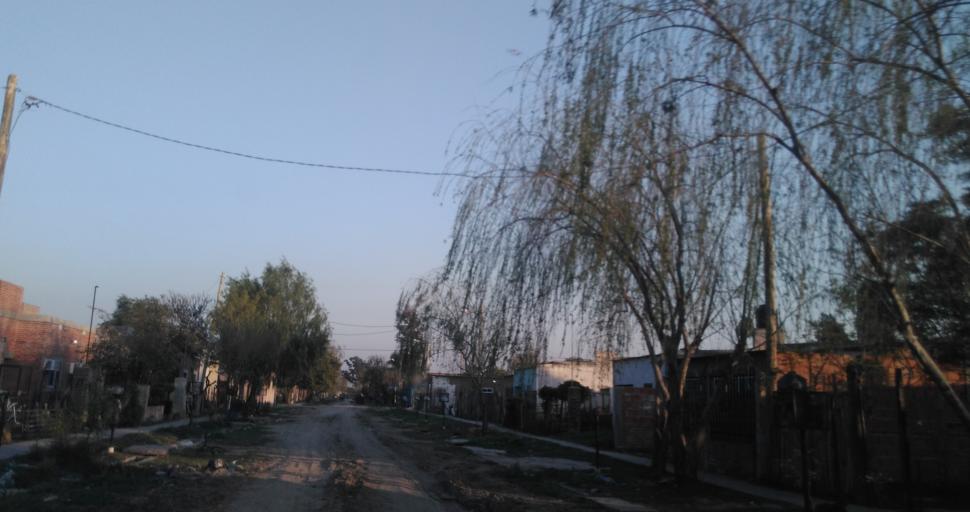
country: AR
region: Chaco
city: Resistencia
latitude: -27.4793
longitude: -59.0113
